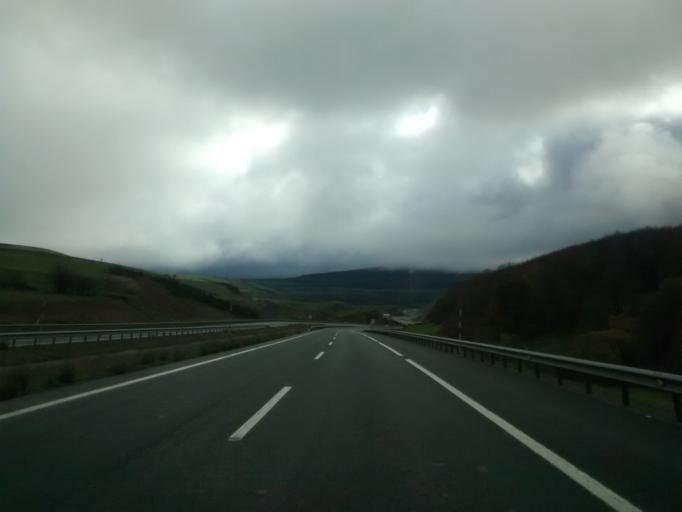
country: ES
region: Cantabria
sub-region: Provincia de Cantabria
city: Villaescusa
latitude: 42.9534
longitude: -4.1504
